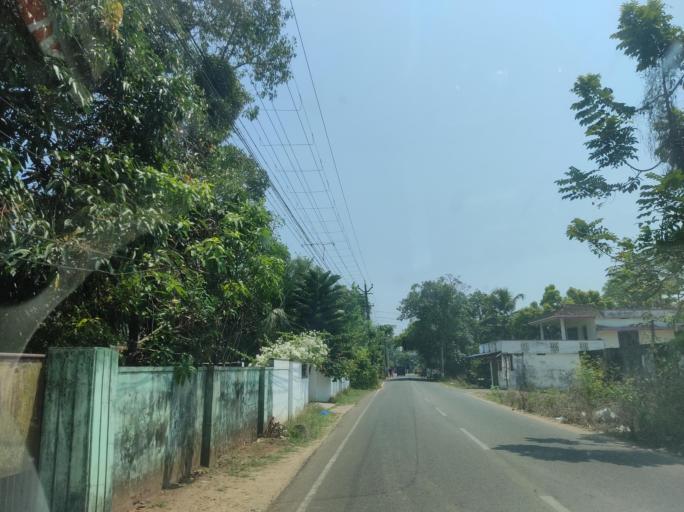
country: IN
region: Kerala
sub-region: Alappuzha
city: Kutiatodu
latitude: 9.8118
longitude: 76.3005
